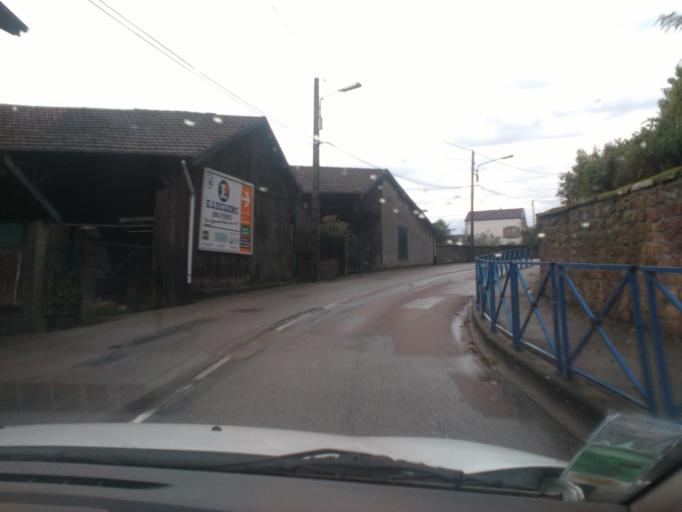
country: FR
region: Lorraine
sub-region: Departement des Vosges
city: Bruyeres
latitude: 48.2123
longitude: 6.7211
